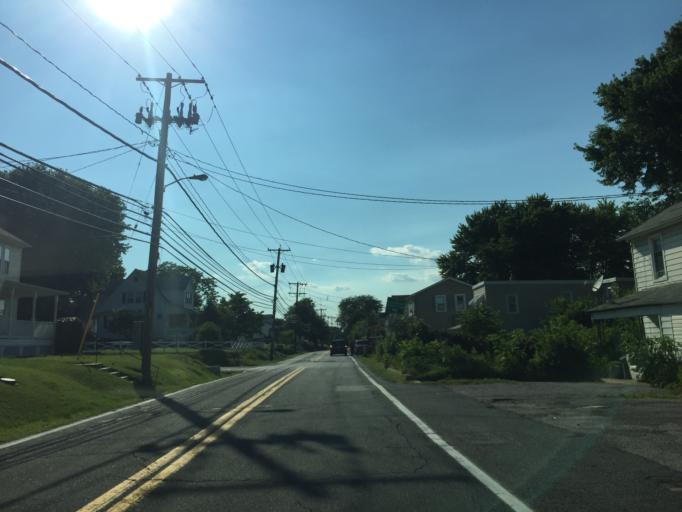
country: US
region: Maryland
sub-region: Baltimore County
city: Rosedale
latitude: 39.2917
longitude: -76.5163
